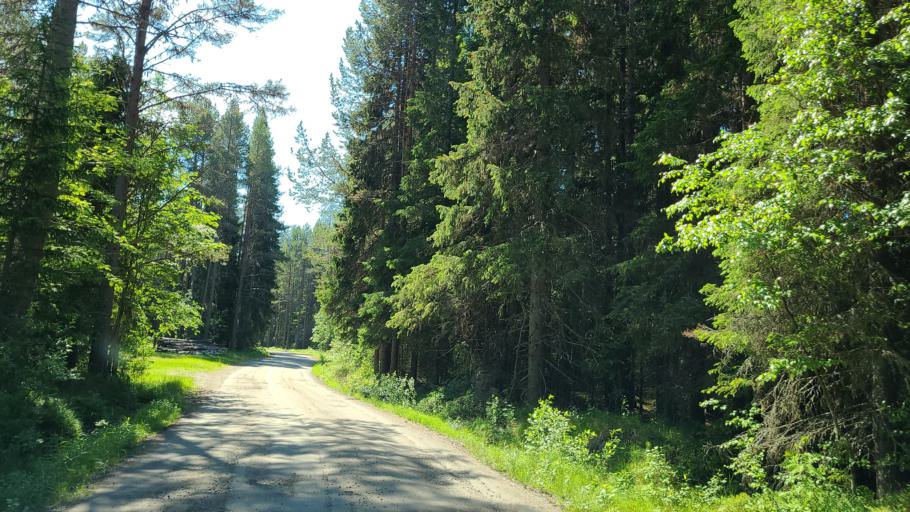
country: SE
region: Vaesterbotten
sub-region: Robertsfors Kommun
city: Robertsfors
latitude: 64.1430
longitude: 20.9606
